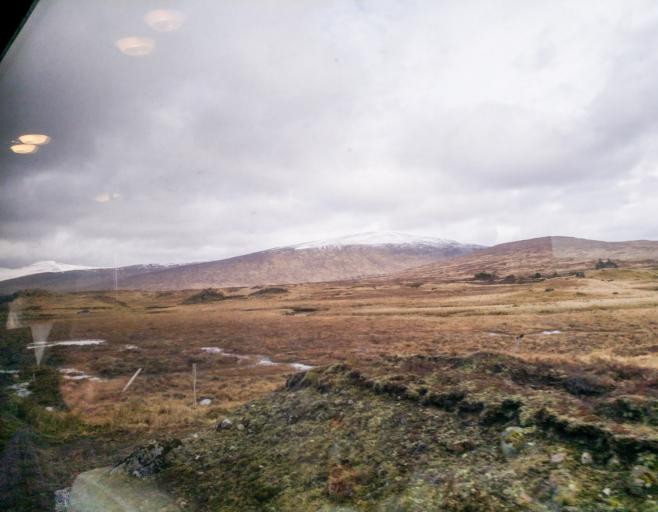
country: GB
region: Scotland
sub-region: Highland
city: Spean Bridge
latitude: 56.7397
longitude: -4.6638
